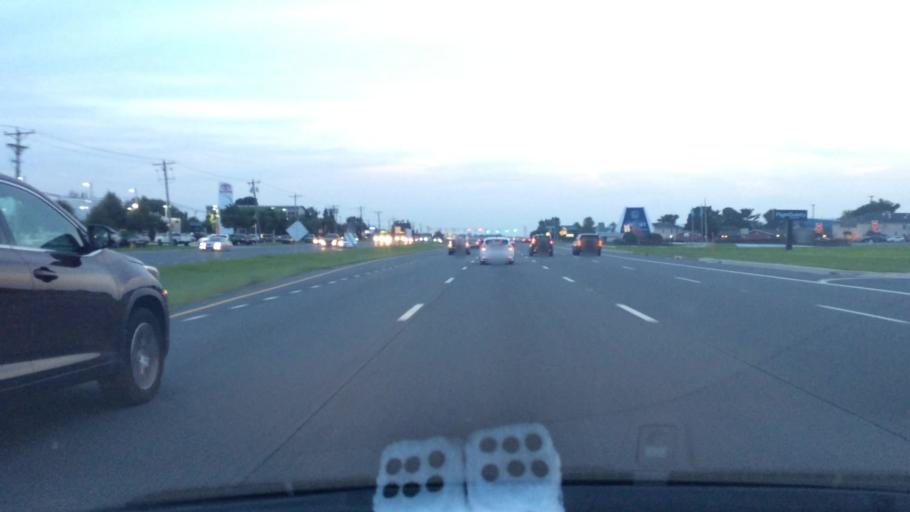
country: US
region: Delaware
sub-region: New Castle County
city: Wilmington Manor
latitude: 39.6757
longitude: -75.5950
